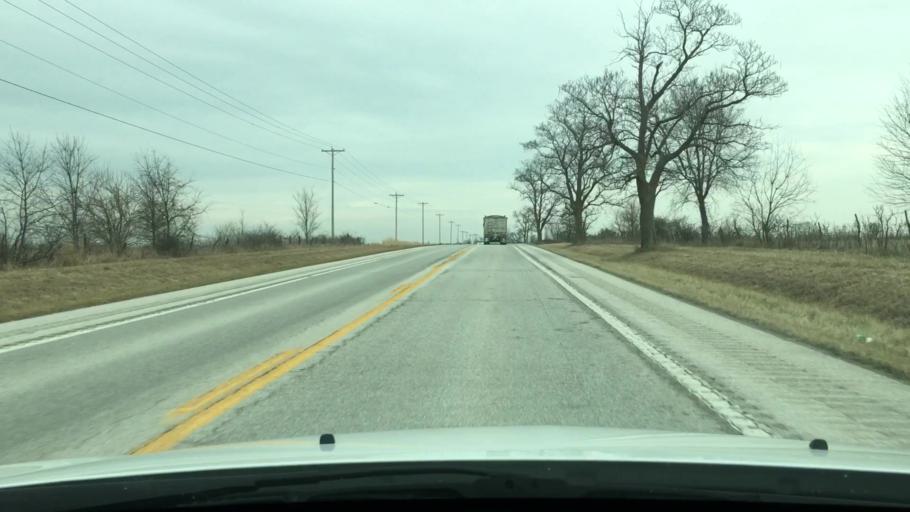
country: US
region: Missouri
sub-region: Pike County
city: Bowling Green
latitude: 39.3443
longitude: -91.2643
